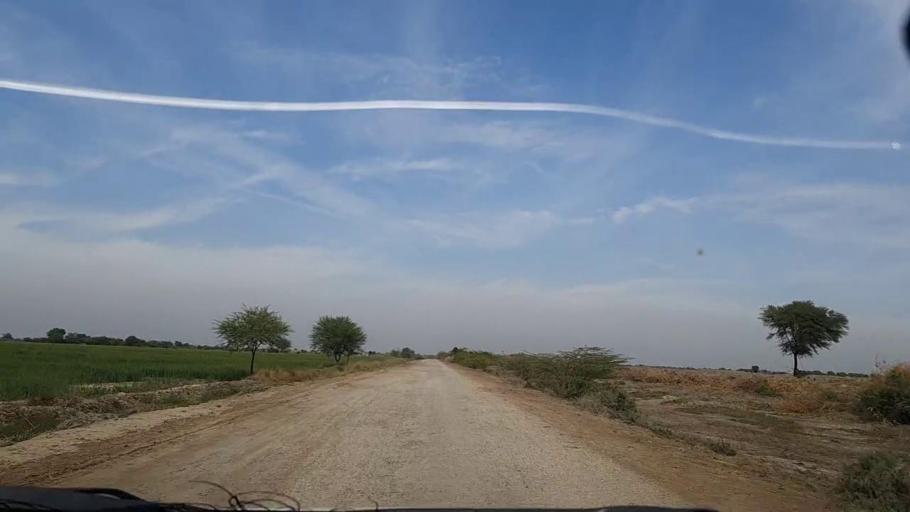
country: PK
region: Sindh
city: Pithoro
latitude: 25.4711
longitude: 69.4568
